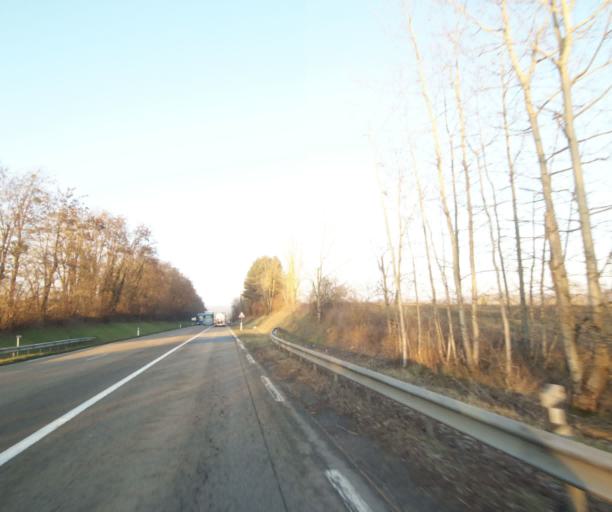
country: FR
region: Champagne-Ardenne
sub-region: Departement de la Haute-Marne
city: Bienville
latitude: 48.5869
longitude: 5.0291
